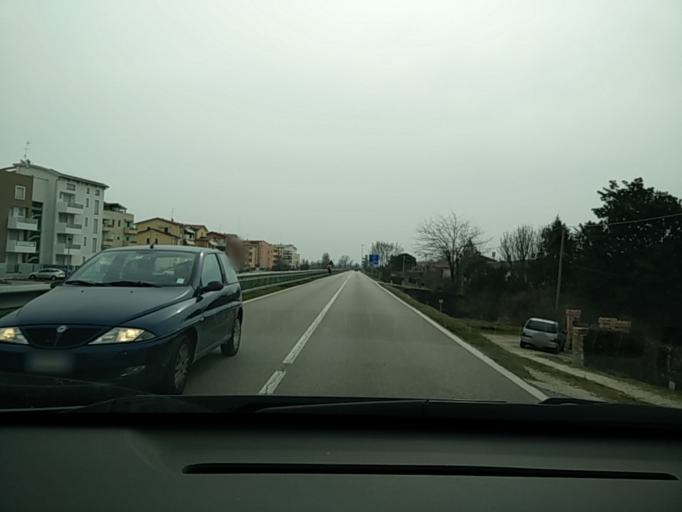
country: IT
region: Veneto
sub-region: Provincia di Venezia
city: Musile di Piave
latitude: 45.6145
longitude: 12.5597
